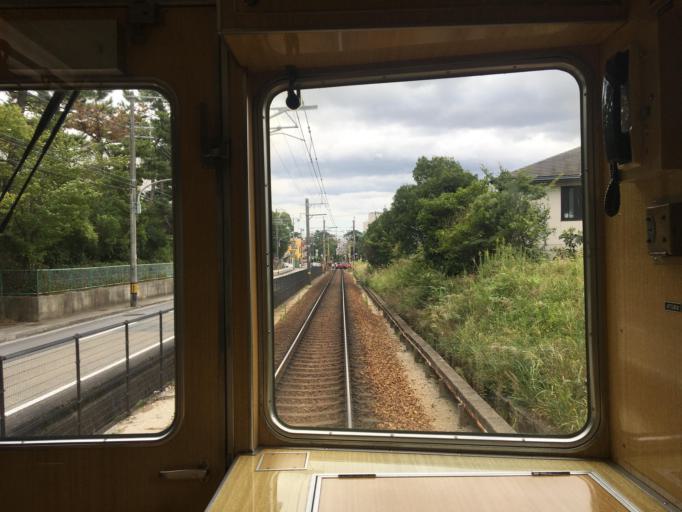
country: JP
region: Hyogo
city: Ashiya
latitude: 34.7551
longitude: 135.3311
